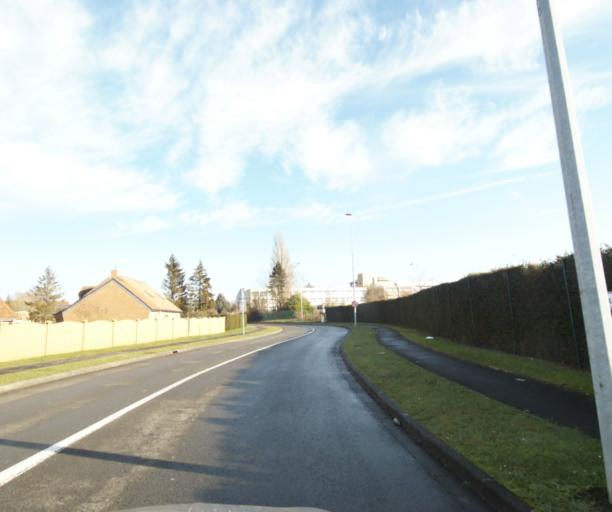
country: FR
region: Nord-Pas-de-Calais
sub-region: Departement du Nord
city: Marly
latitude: 50.3383
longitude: 3.5538
